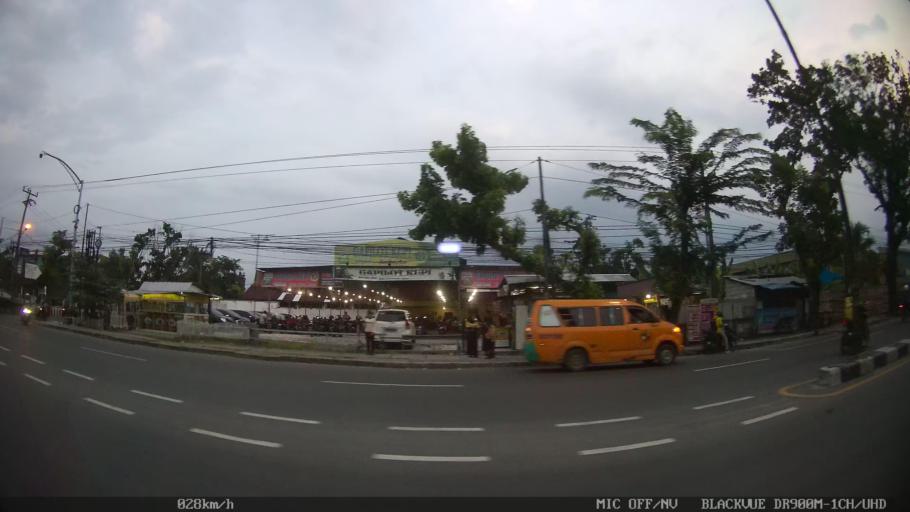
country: ID
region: North Sumatra
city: Sunggal
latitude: 3.5932
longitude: 98.6208
